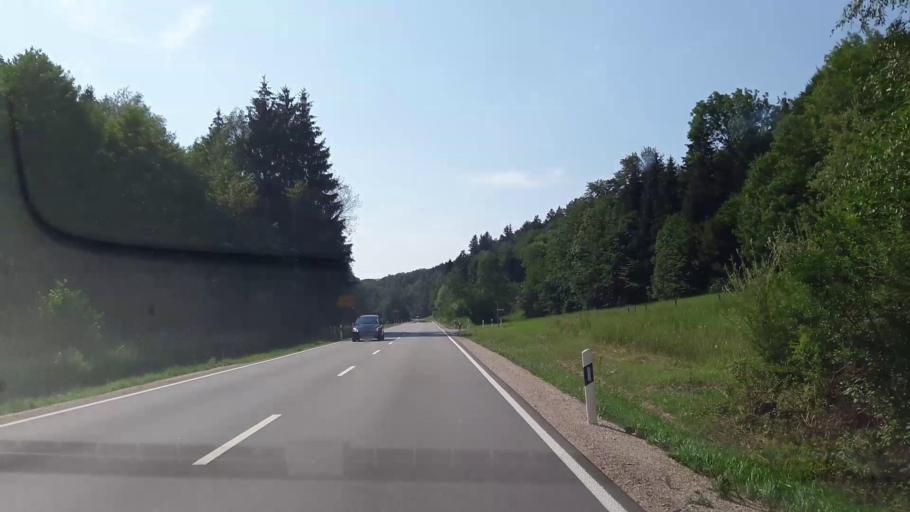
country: DE
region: Bavaria
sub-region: Upper Bavaria
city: Surberg
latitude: 47.8655
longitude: 12.7289
